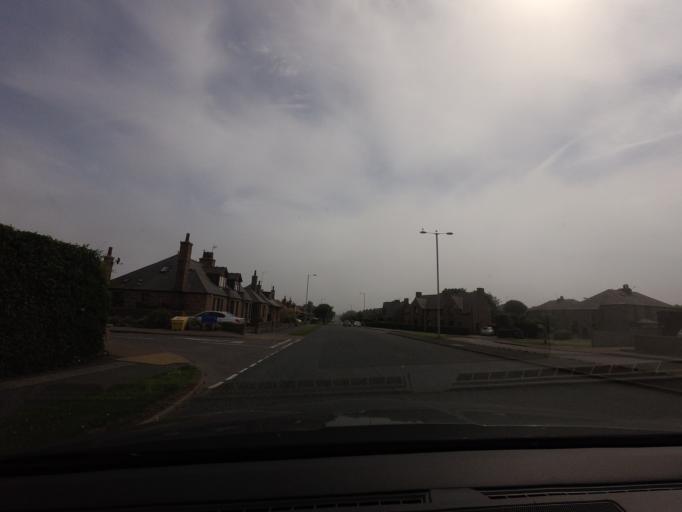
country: GB
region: Scotland
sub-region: Aberdeenshire
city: Peterhead
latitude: 57.5068
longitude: -1.7989
